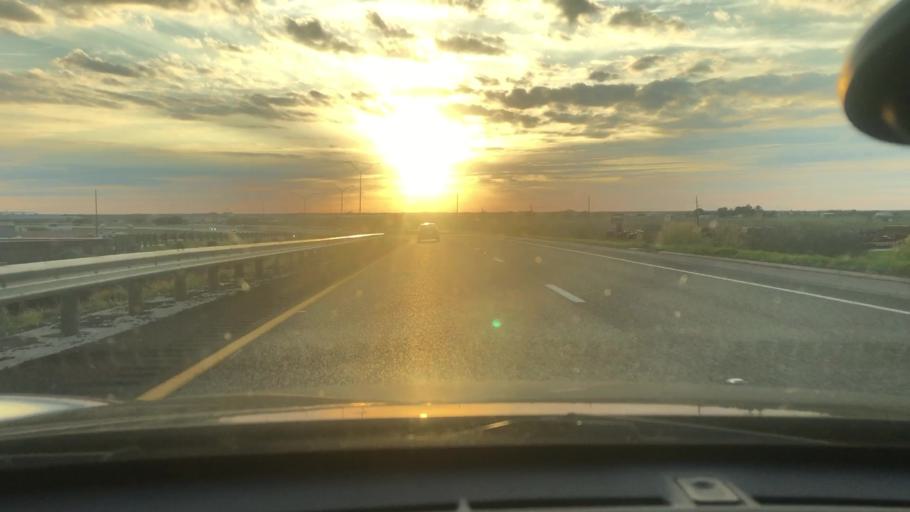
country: US
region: Texas
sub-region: Wharton County
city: El Campo
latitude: 29.1741
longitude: -96.3046
